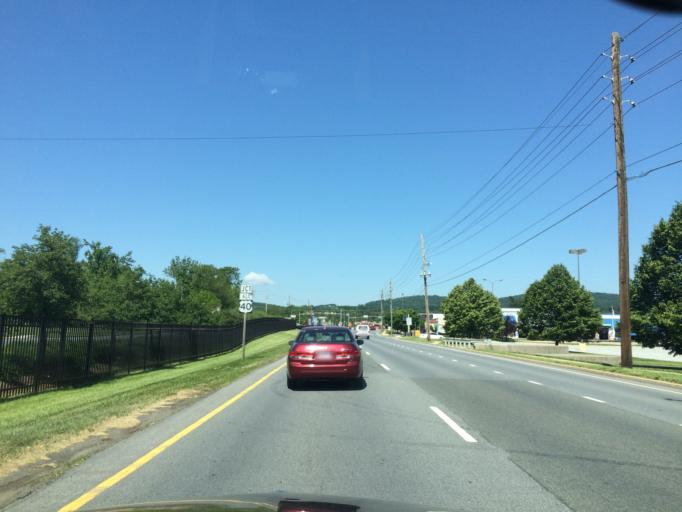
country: US
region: Maryland
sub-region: Frederick County
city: Braddock Heights
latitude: 39.4192
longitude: -77.4581
